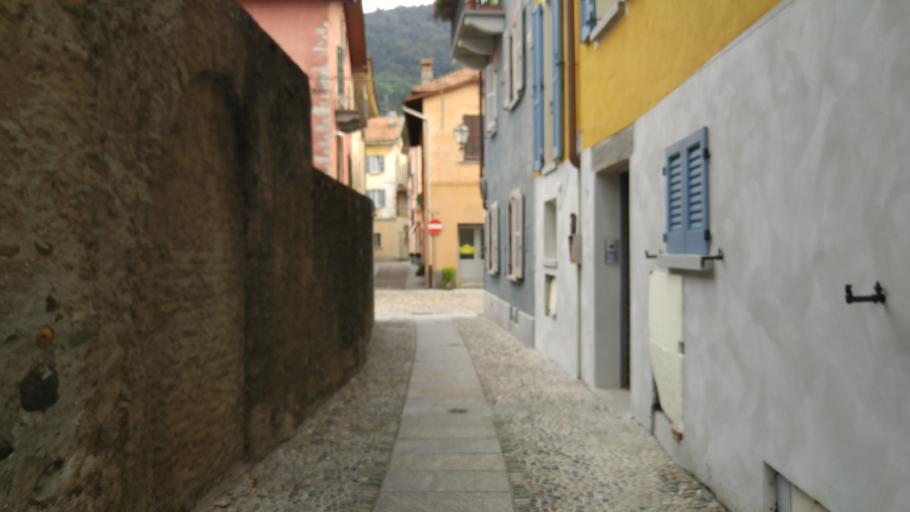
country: IT
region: Piedmont
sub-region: Provincia Verbano-Cusio-Ossola
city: Cannobio
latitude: 46.0619
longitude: 8.6952
